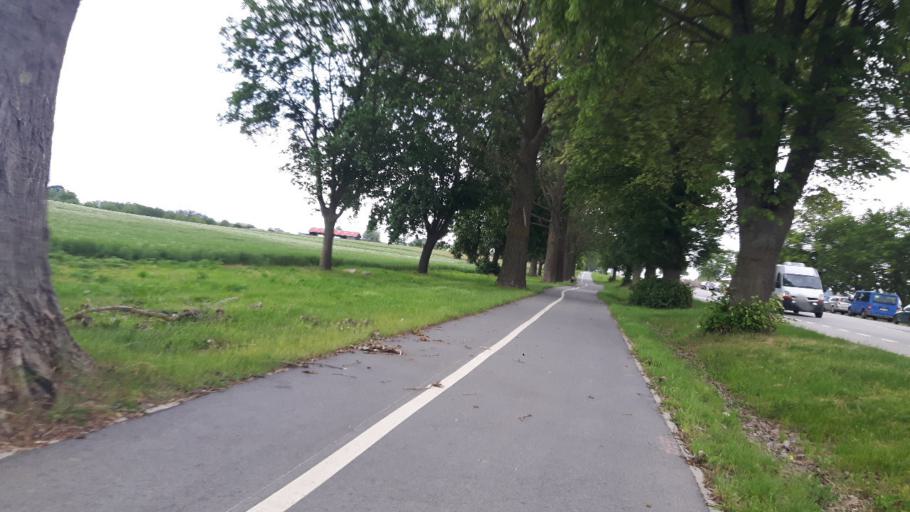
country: PL
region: West Pomeranian Voivodeship
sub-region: Powiat policki
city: Kolbaskowo
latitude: 53.3452
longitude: 14.4505
